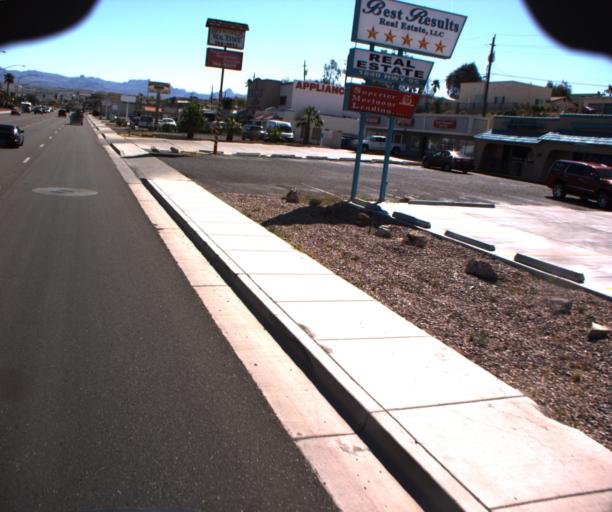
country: US
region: Arizona
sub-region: Mohave County
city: Bullhead City
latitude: 35.1198
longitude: -114.5920
